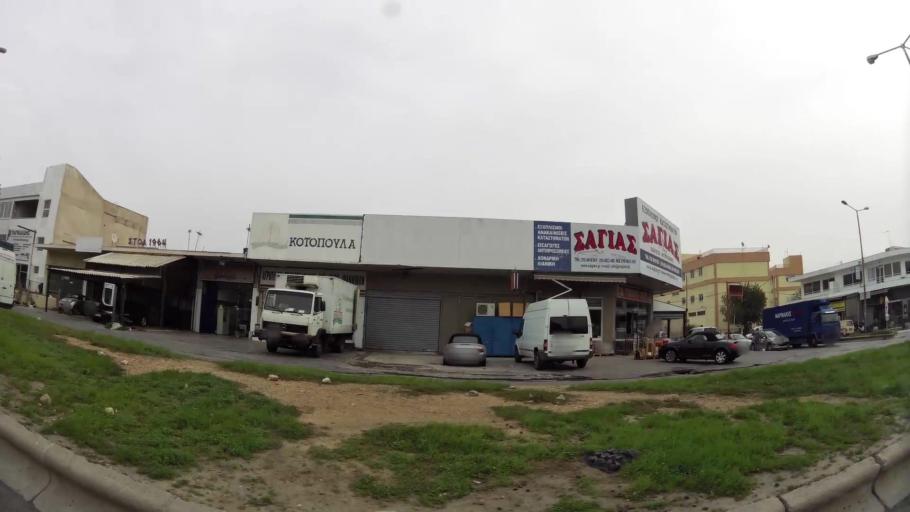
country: GR
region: Attica
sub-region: Nomarchia Athinas
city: Tavros
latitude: 37.9614
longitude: 23.6829
